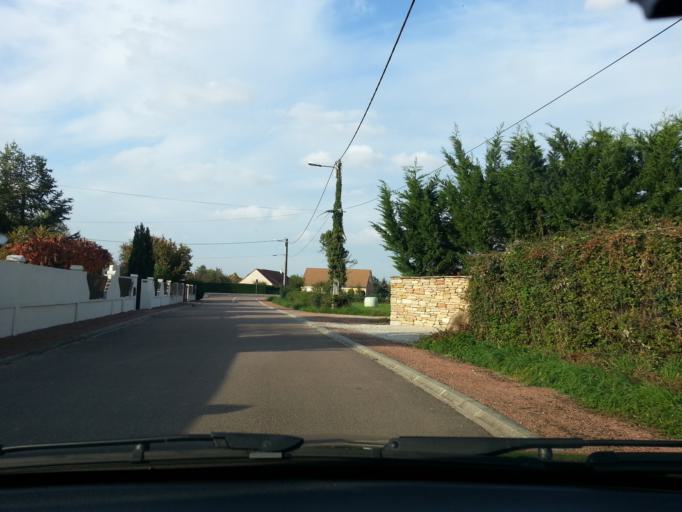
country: FR
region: Bourgogne
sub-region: Departement de Saone-et-Loire
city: Chatenoy-le-Royal
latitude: 46.7775
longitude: 4.8051
